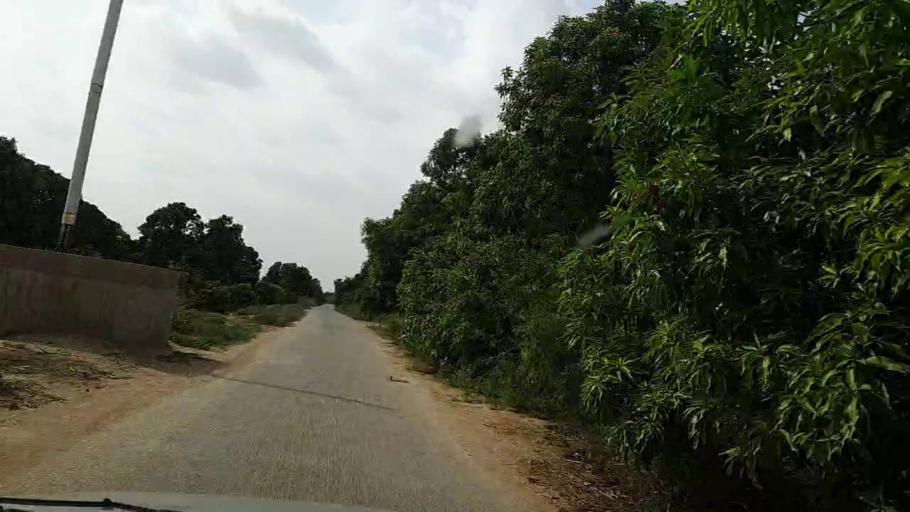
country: PK
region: Sindh
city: Kotri
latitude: 25.2508
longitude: 68.2587
